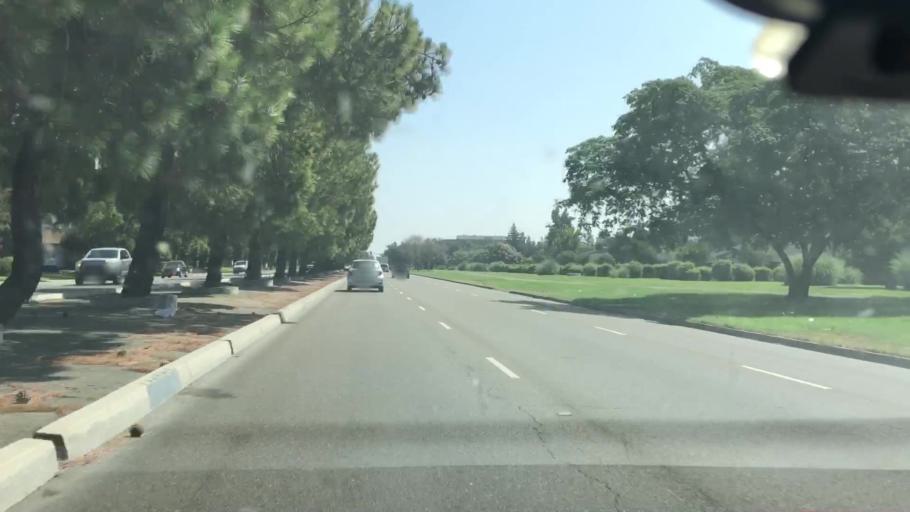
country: US
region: California
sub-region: San Joaquin County
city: Lincoln Village
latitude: 37.9863
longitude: -121.3325
